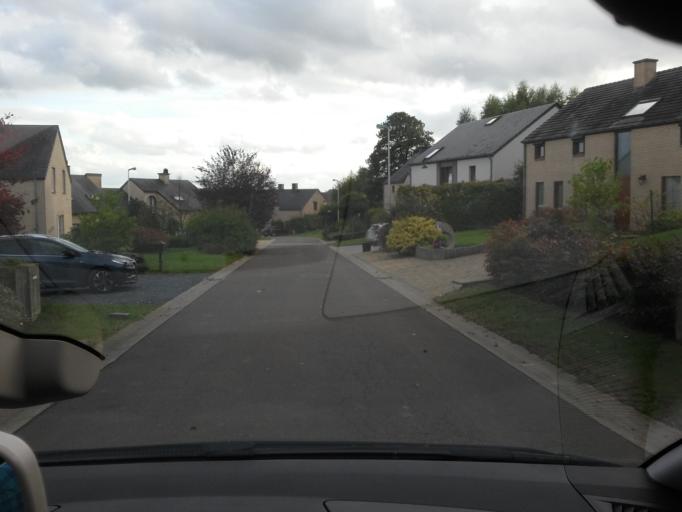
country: BE
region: Wallonia
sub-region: Province du Luxembourg
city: Arlon
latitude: 49.6995
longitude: 5.7692
